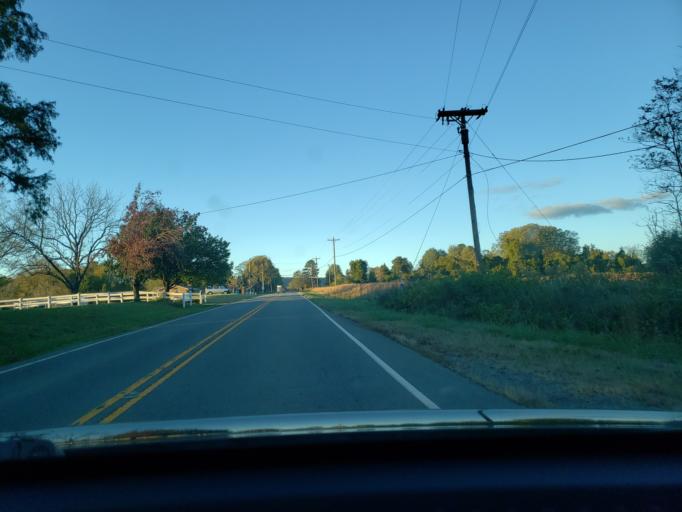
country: US
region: North Carolina
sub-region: Stokes County
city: Danbury
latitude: 36.3446
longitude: -80.2203
